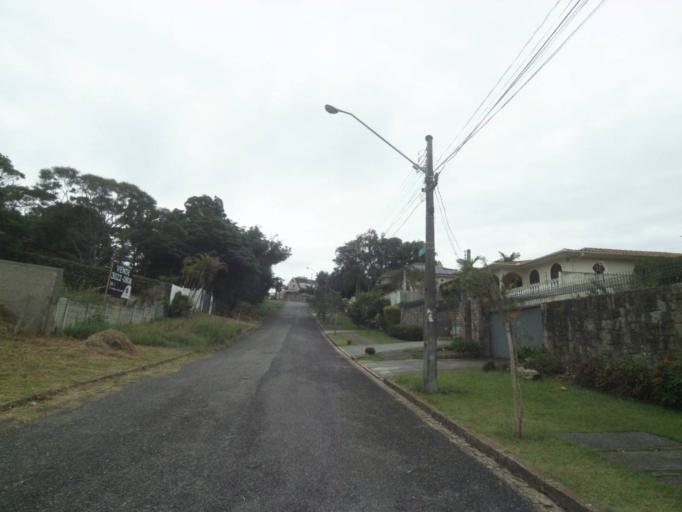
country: BR
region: Parana
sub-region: Curitiba
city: Curitiba
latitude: -25.4040
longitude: -49.2880
